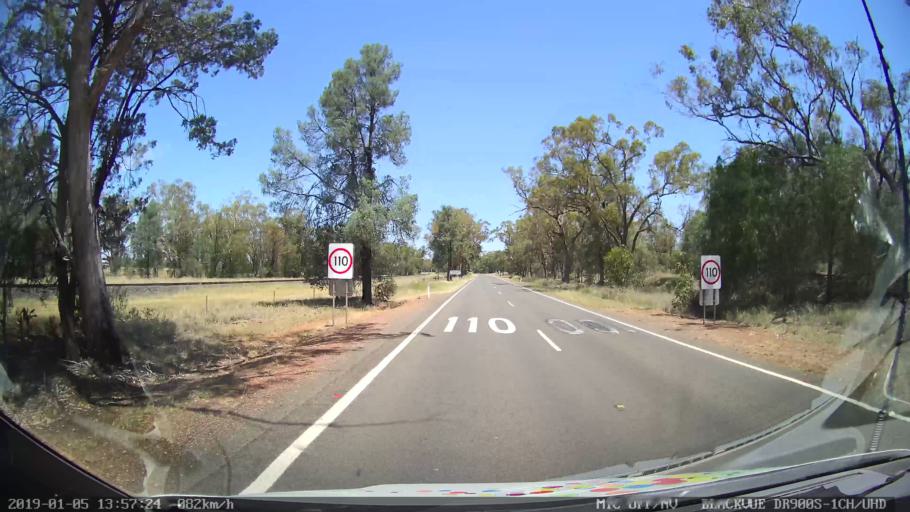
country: AU
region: New South Wales
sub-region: Gunnedah
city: Gunnedah
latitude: -31.1271
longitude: 150.2745
